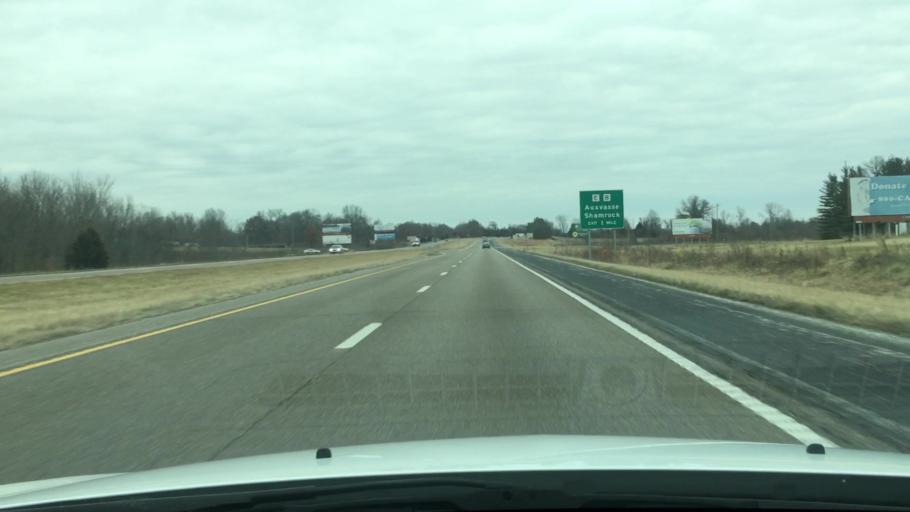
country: US
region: Missouri
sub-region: Callaway County
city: Fulton
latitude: 39.0009
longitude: -91.8930
